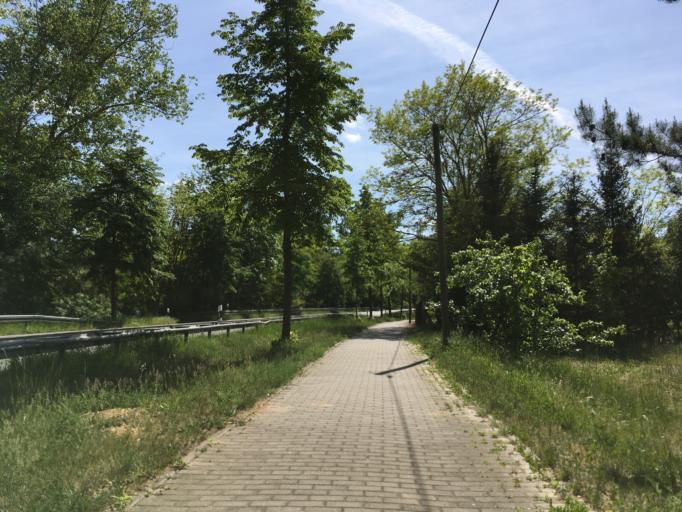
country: DE
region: Brandenburg
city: Oderberg
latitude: 52.8405
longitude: 14.1107
